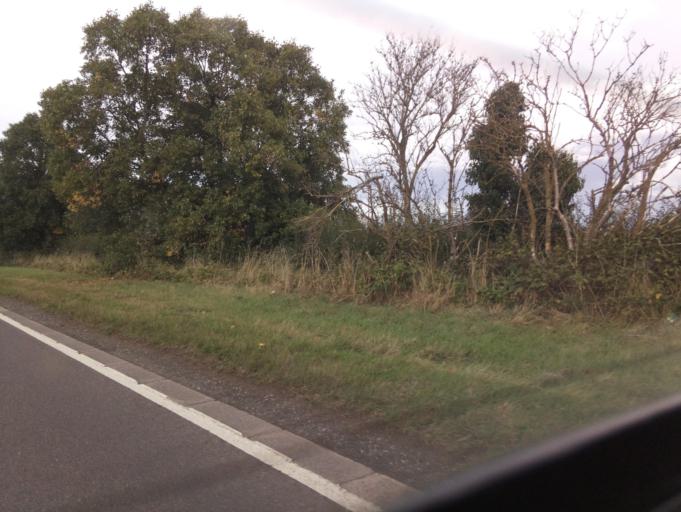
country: GB
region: England
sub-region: Telford and Wrekin
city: Madeley
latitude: 52.5932
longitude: -2.3989
